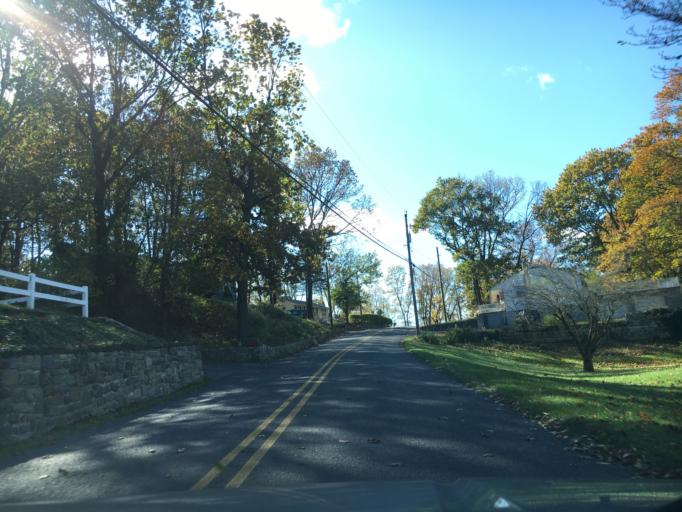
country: US
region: Pennsylvania
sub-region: Berks County
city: South Temple
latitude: 40.4017
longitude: -75.8886
